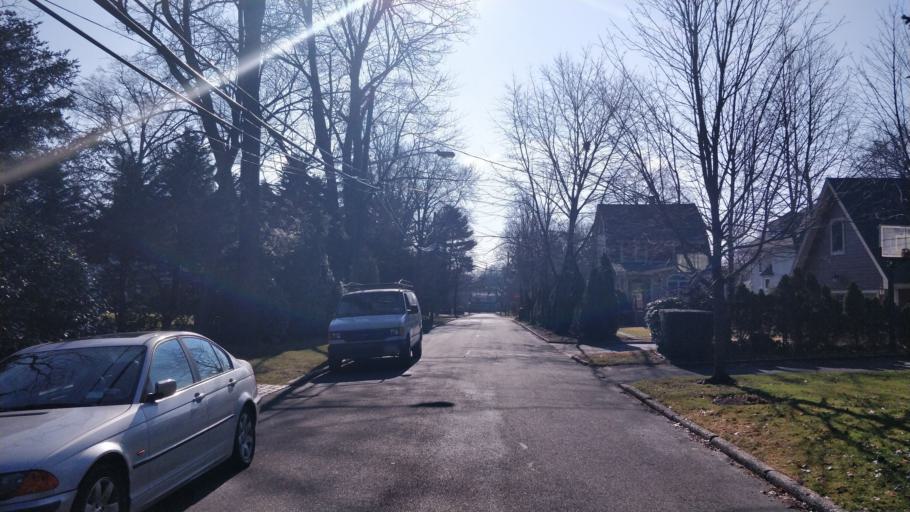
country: US
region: New York
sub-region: Nassau County
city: Sea Cliff
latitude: 40.8508
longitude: -73.6389
